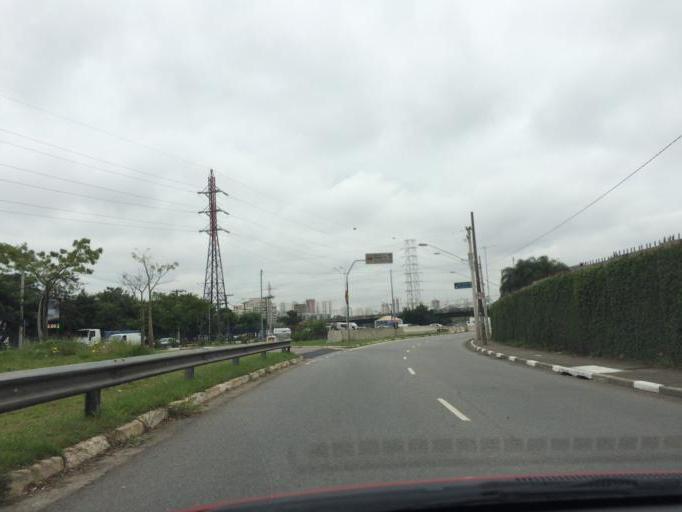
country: BR
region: Sao Paulo
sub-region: Osasco
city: Osasco
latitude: -23.5503
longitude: -46.7325
